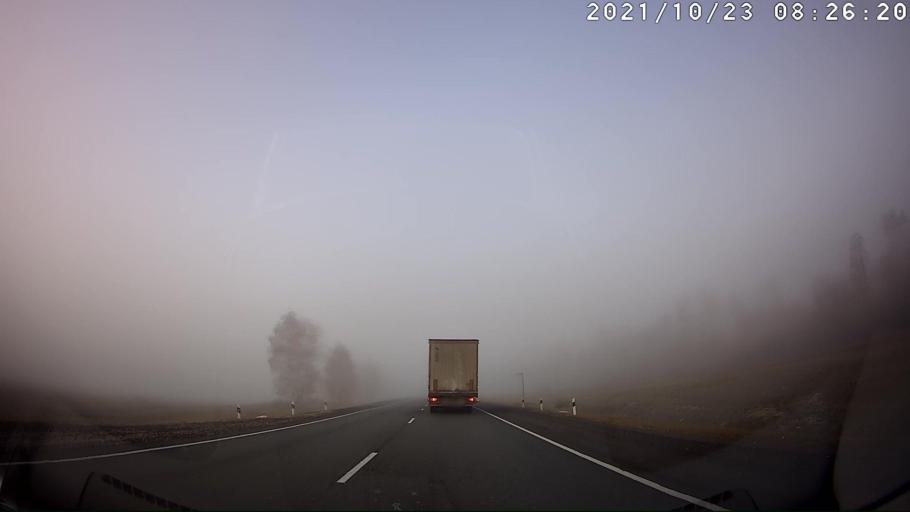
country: RU
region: Saratov
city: Sennoy
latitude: 52.1334
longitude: 46.8663
